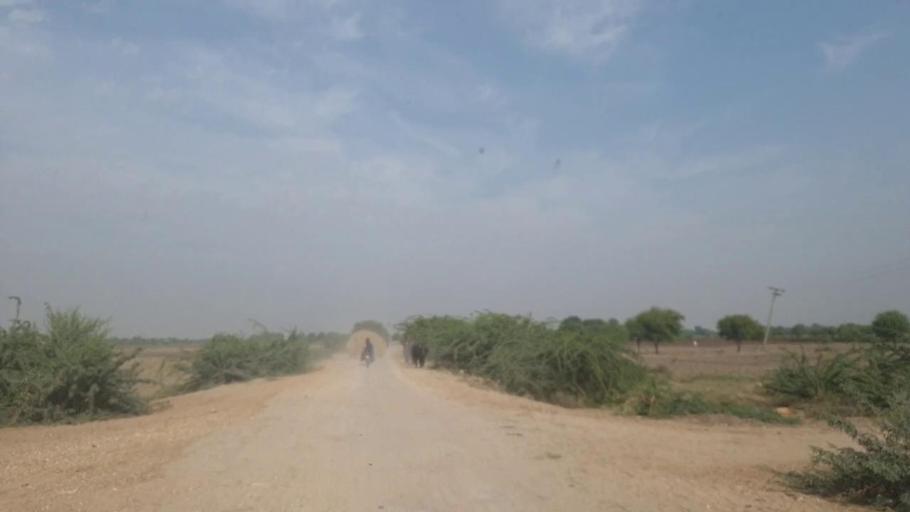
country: PK
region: Sindh
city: Tando Bago
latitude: 24.9290
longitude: 68.9880
